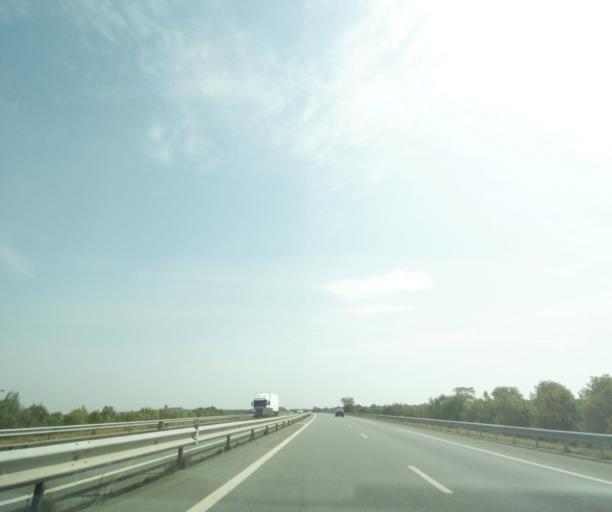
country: FR
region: Poitou-Charentes
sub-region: Departement des Deux-Sevres
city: La Creche
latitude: 46.3535
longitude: -0.3343
